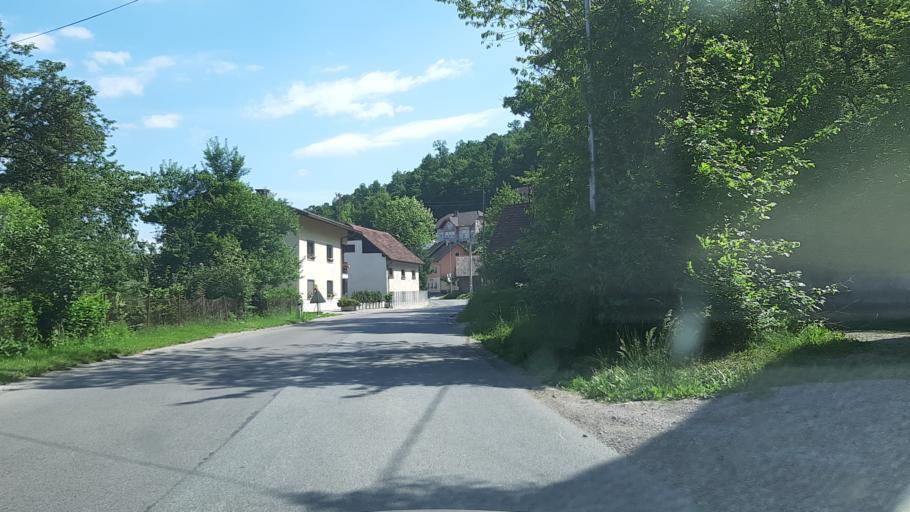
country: SI
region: Brezovica
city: Notranje Gorice
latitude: 45.9683
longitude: 14.4147
